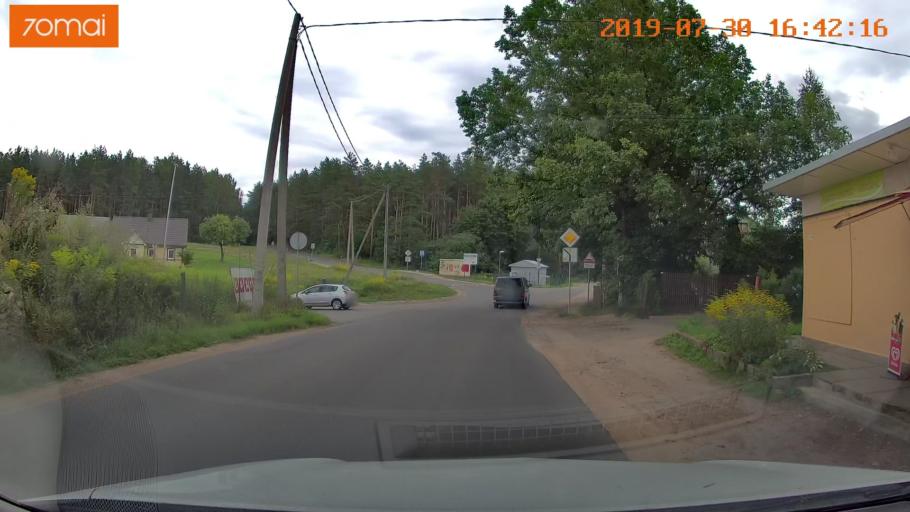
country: LT
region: Vilnius County
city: Rasos
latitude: 54.7155
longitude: 25.3543
